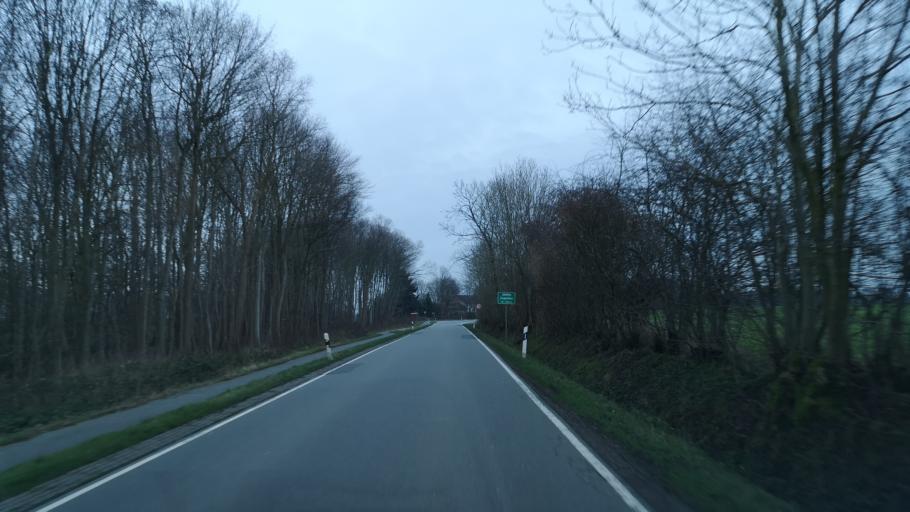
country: DE
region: Schleswig-Holstein
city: Satrup
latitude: 54.7017
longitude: 9.6359
